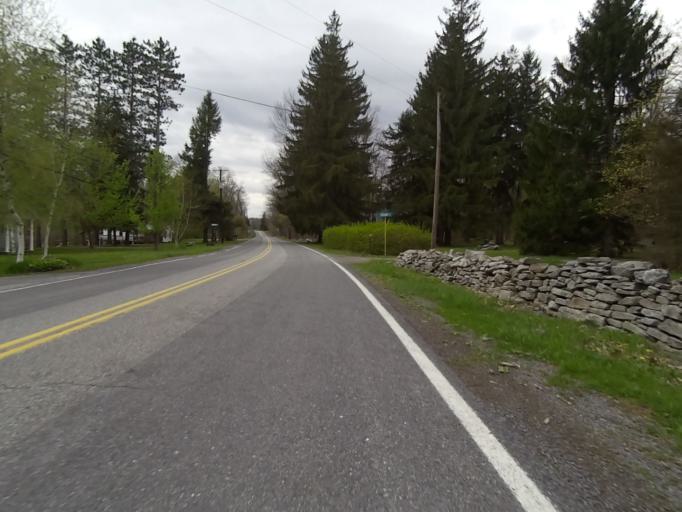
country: US
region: Pennsylvania
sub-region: Centre County
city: Stormstown
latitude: 40.9126
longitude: -78.0727
